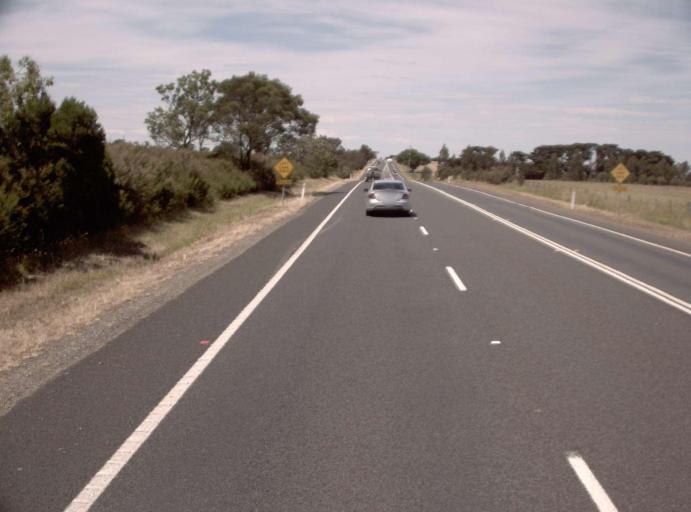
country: AU
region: Victoria
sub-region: Wellington
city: Heyfield
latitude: -38.1257
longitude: 146.8404
